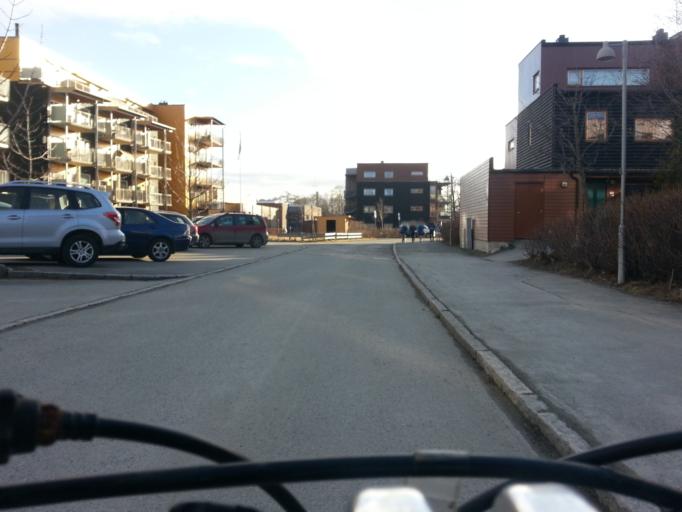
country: NO
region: Sor-Trondelag
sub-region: Trondheim
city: Trondheim
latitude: 63.4490
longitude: 10.4444
